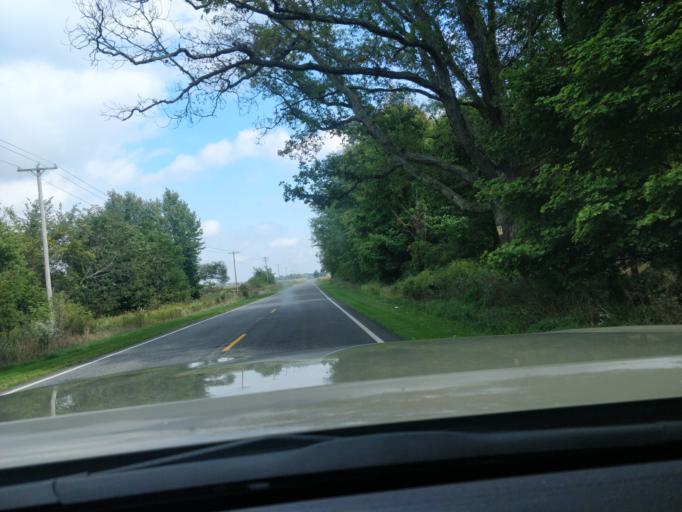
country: US
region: Michigan
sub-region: Ionia County
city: Saranac
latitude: 42.8862
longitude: -85.2364
